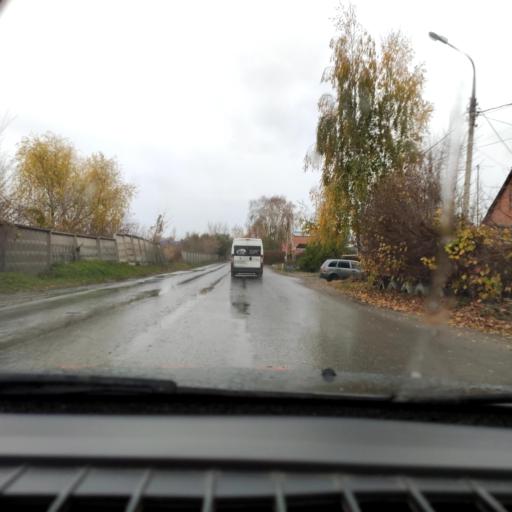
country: RU
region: Samara
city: Tol'yatti
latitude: 53.5390
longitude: 49.4252
